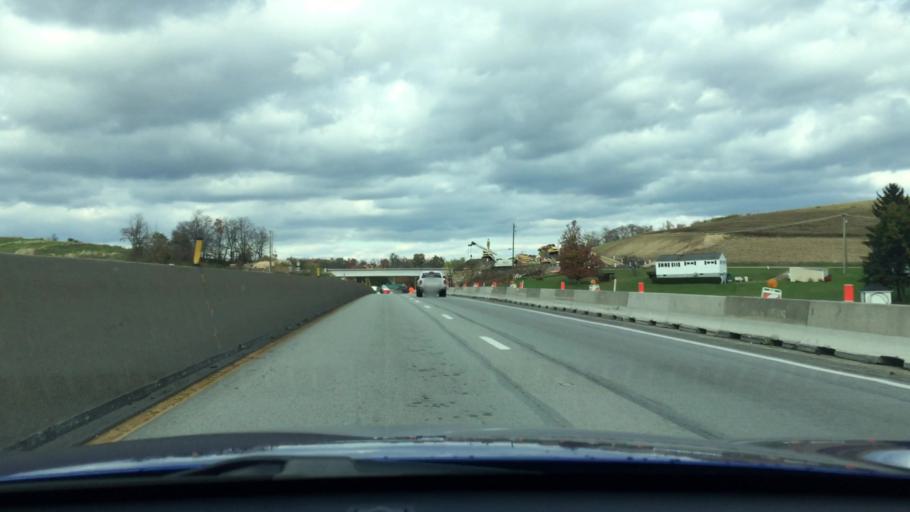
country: US
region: Pennsylvania
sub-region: Westmoreland County
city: West Newton
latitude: 40.1811
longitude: -79.7111
